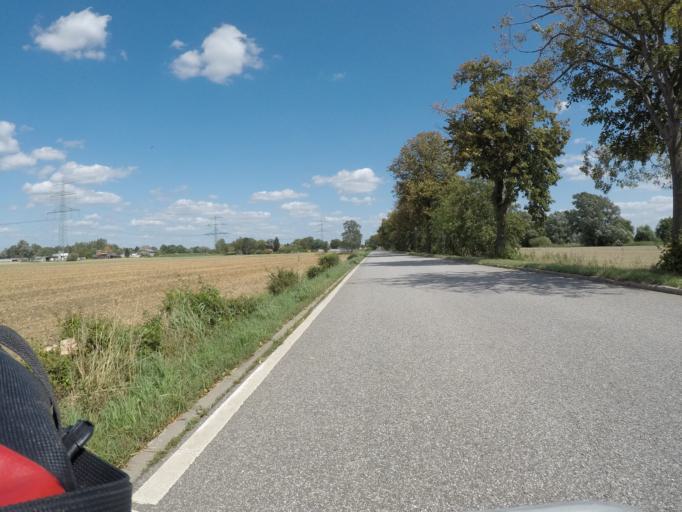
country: DE
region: Lower Saxony
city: Stelle
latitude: 53.4611
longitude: 10.1139
